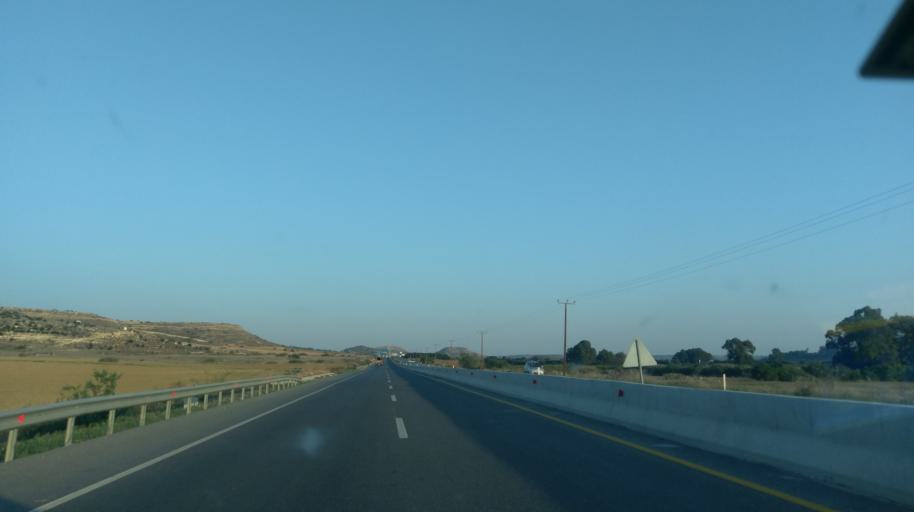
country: CY
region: Lefkosia
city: Peristerona
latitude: 35.1960
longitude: 33.0965
